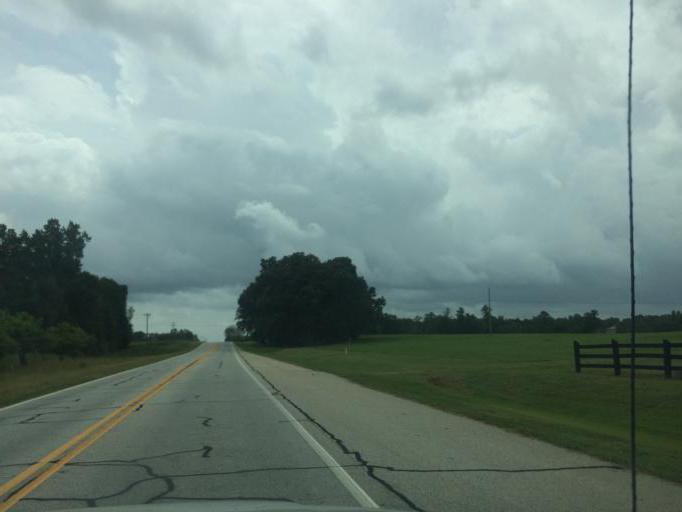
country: US
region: Georgia
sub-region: Hart County
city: Hartwell
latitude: 34.2436
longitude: -82.8994
